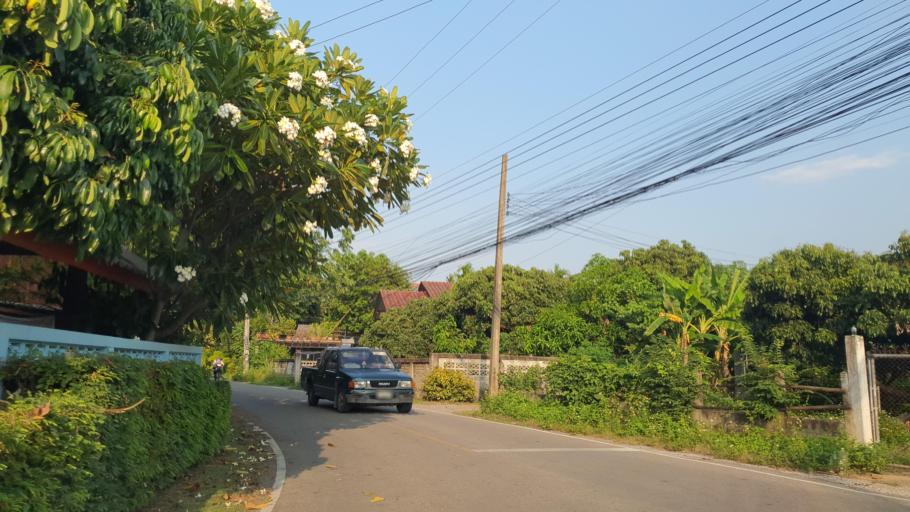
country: TH
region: Chiang Mai
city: San Pa Tong
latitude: 18.6348
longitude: 98.8526
